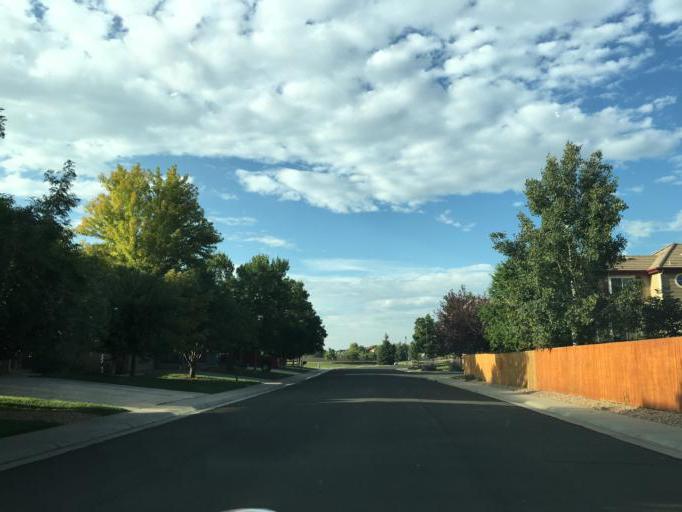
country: US
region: Colorado
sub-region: Adams County
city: Northglenn
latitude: 39.9478
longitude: -104.9550
